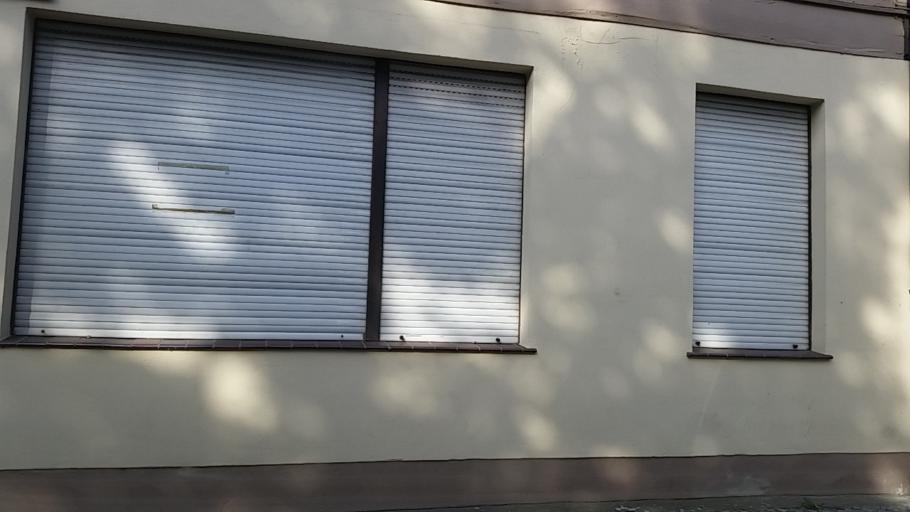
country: DE
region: Saxony-Anhalt
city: Salzwedel
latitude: 52.8494
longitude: 11.1584
